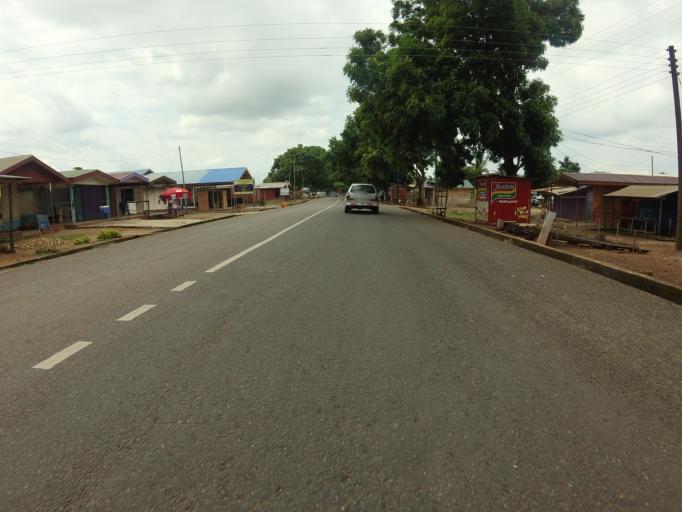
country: GH
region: Volta
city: Ho
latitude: 6.6157
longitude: 0.4920
